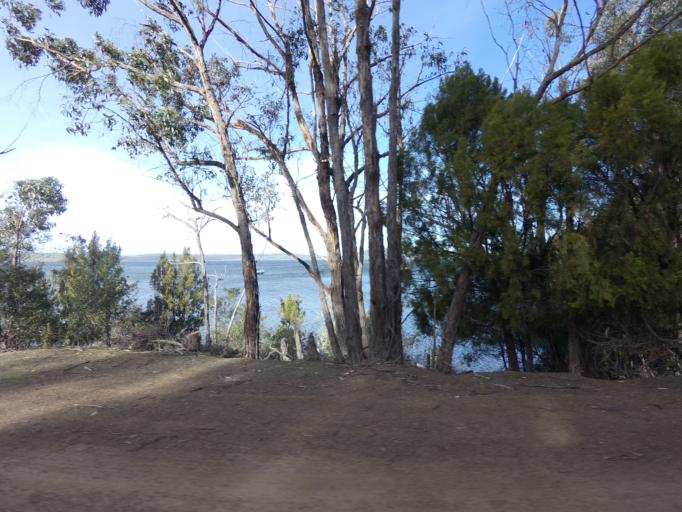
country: AU
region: Tasmania
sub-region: Kingborough
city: Kettering
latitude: -43.1159
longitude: 147.2709
